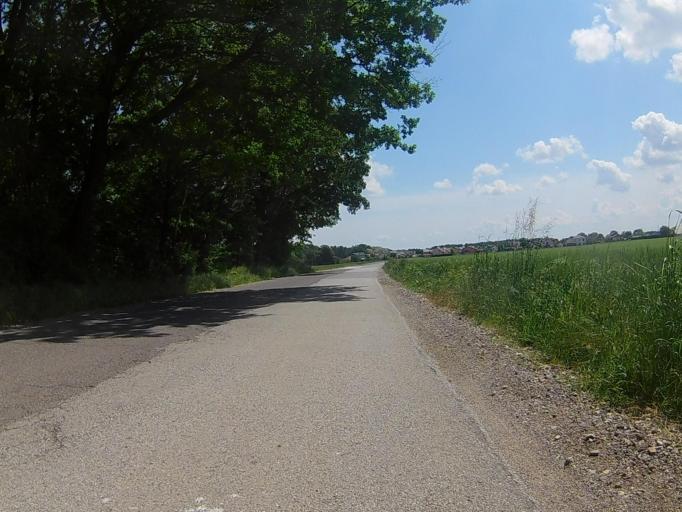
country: SI
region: Hoce-Slivnica
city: Rogoza
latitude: 46.4931
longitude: 15.6873
